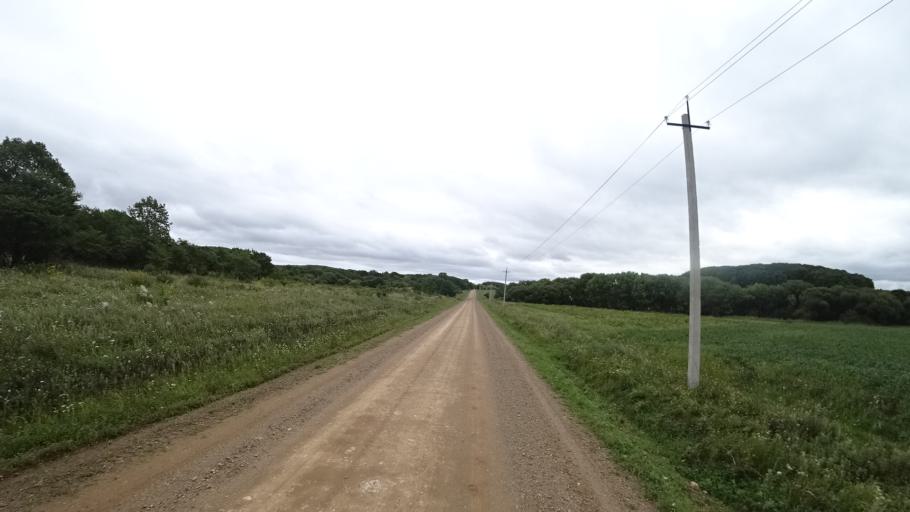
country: RU
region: Primorskiy
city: Chernigovka
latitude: 44.4672
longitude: 132.5862
